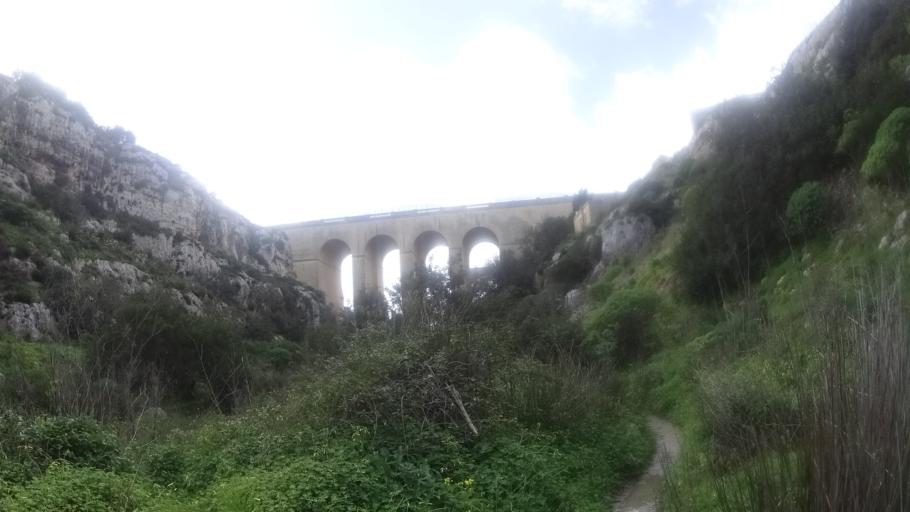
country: MT
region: Il-Mosta
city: Mosta
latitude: 35.9190
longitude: 14.4273
